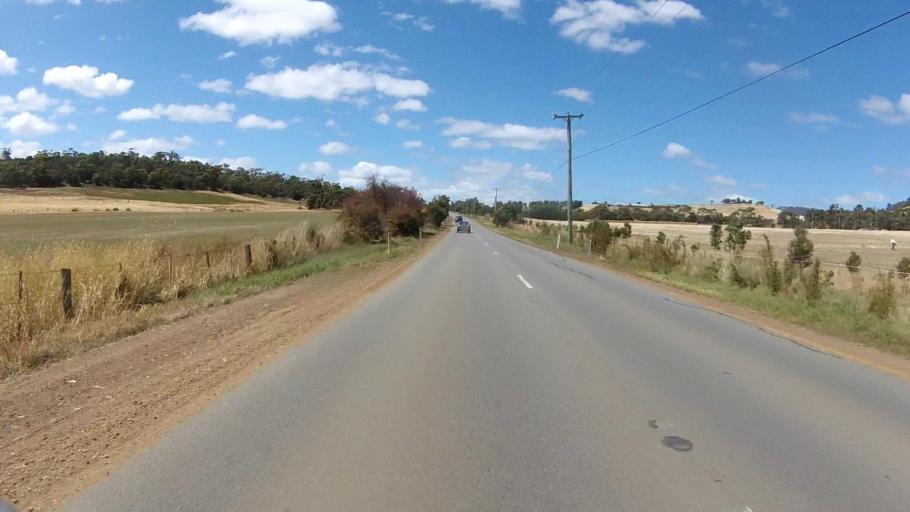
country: AU
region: Tasmania
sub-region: Clarence
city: Cambridge
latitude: -42.8177
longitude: 147.4373
